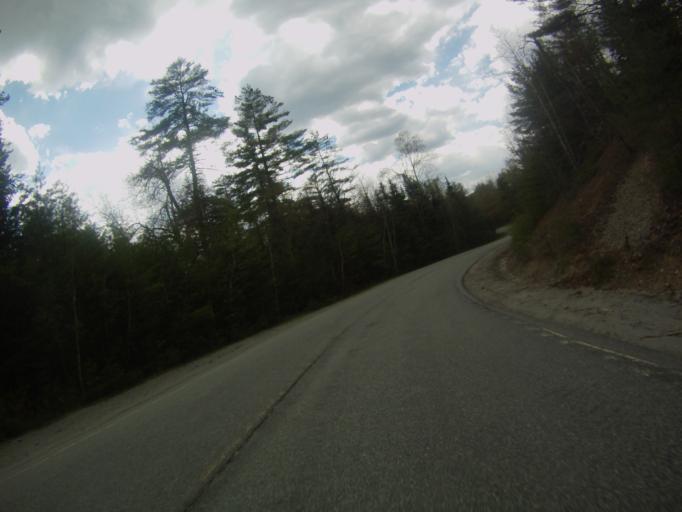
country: US
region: New York
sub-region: Essex County
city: Mineville
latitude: 44.0748
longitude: -73.6357
